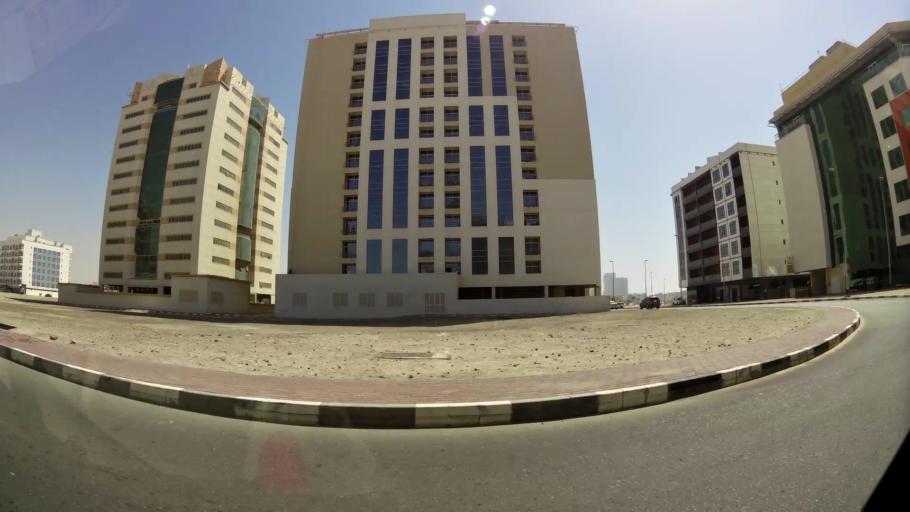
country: AE
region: Dubai
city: Dubai
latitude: 25.1108
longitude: 55.1966
